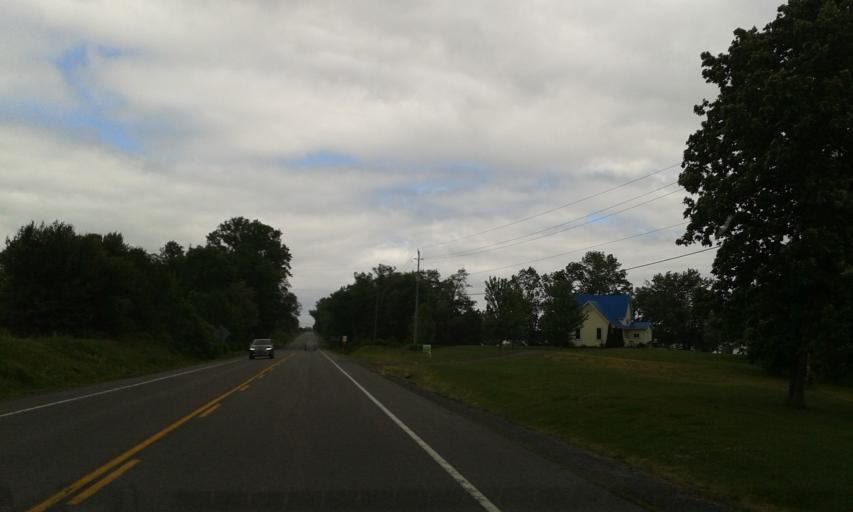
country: CA
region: Ontario
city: Picton
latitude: 44.0500
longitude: -77.0452
